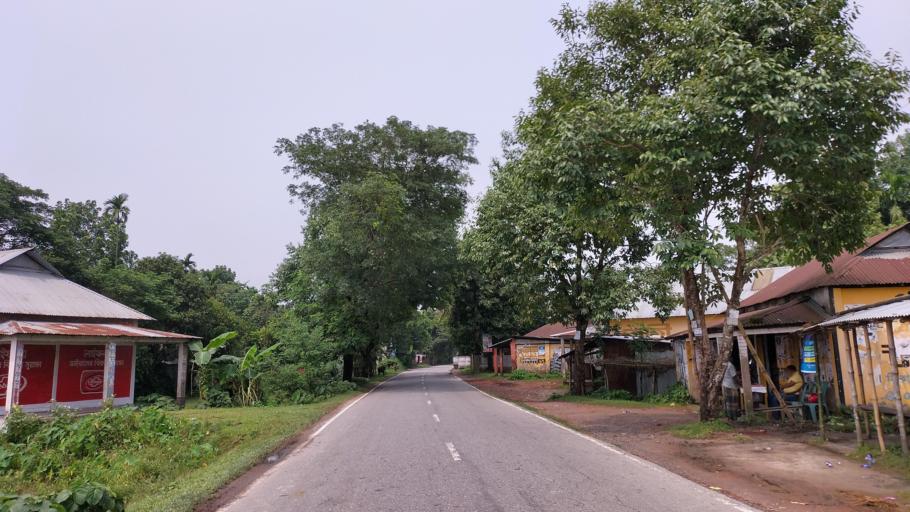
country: BD
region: Dhaka
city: Netrakona
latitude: 24.9045
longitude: 90.7650
